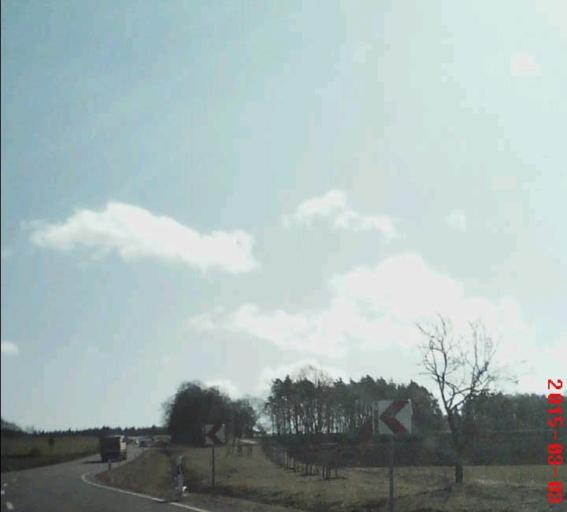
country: DE
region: Thuringia
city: Rottenbach
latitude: 50.7406
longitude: 11.1586
